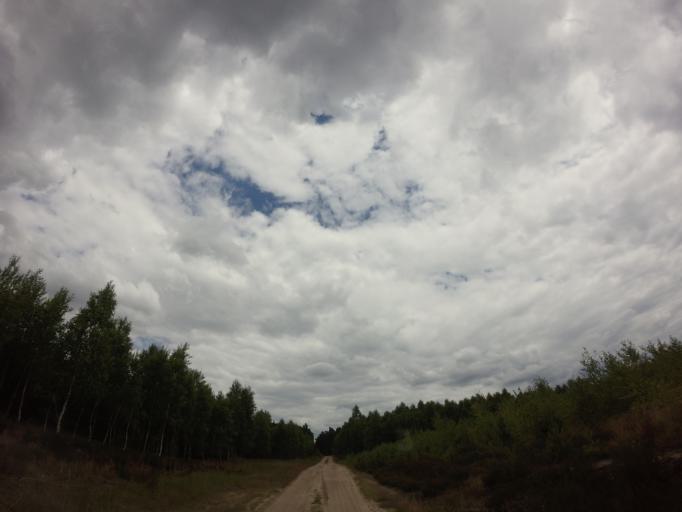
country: PL
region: West Pomeranian Voivodeship
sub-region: Powiat choszczenski
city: Drawno
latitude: 53.1549
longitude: 15.7244
